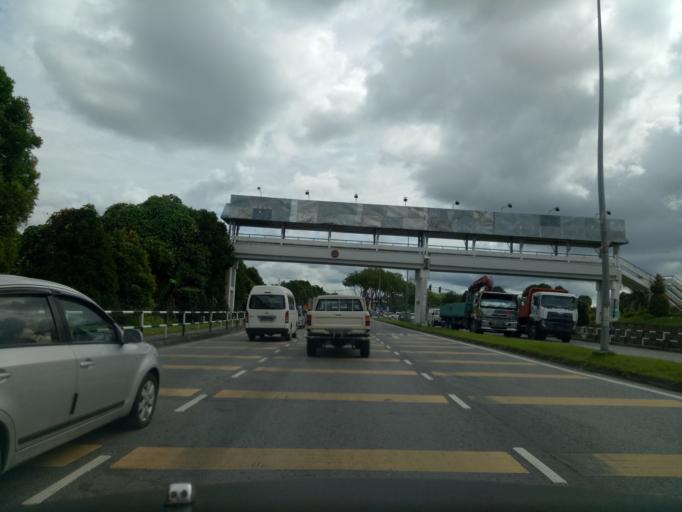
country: MY
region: Sarawak
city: Kuching
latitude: 1.5466
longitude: 110.3828
